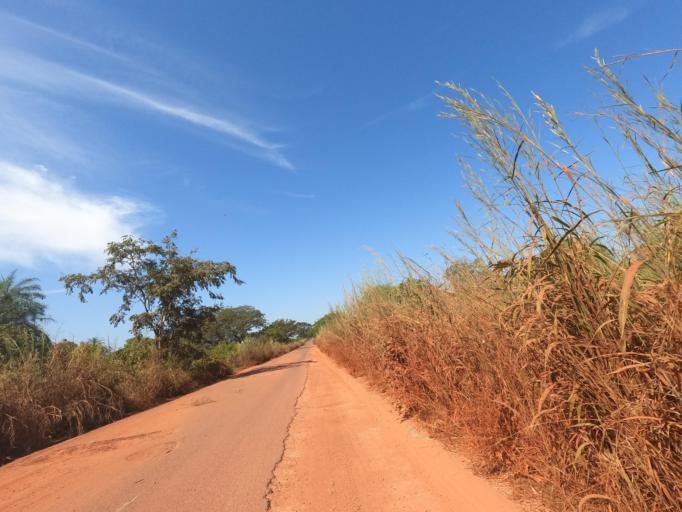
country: SN
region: Ziguinchor
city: Adeane
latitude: 12.3948
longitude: -15.8914
